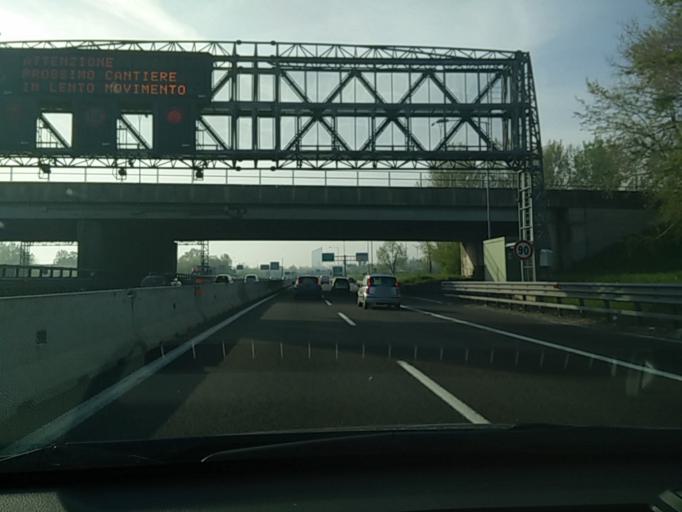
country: IT
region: Emilia-Romagna
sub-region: Provincia di Bologna
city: Quarto Inferiore
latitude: 44.5152
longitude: 11.3767
